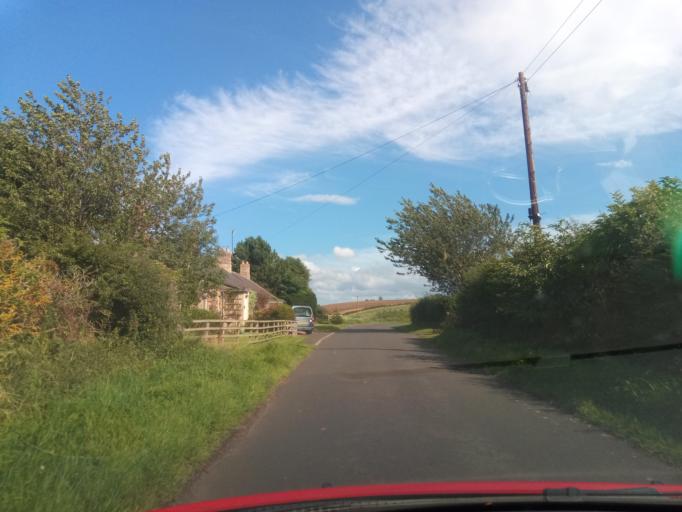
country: GB
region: Scotland
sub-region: The Scottish Borders
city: Coldstream
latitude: 55.6340
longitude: -2.1778
